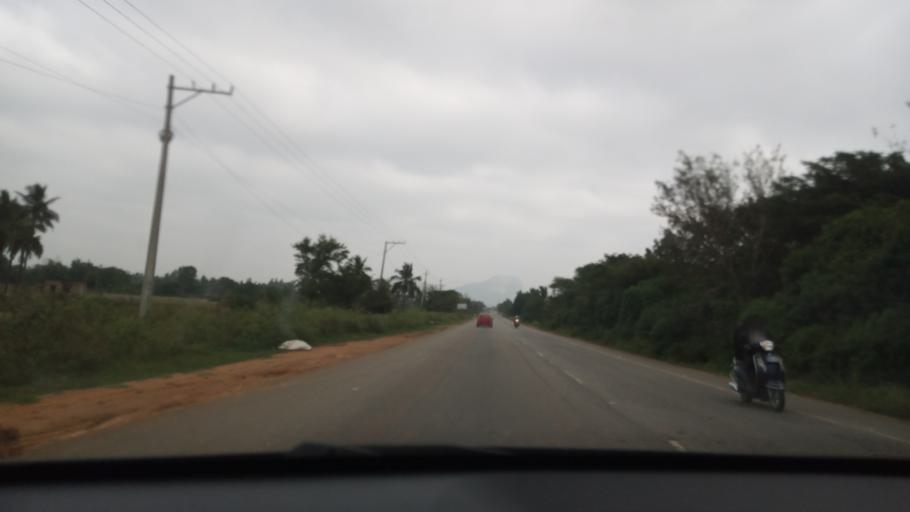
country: IN
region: Karnataka
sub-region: Chikkaballapur
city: Chintamani
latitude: 13.2970
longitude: 77.9681
